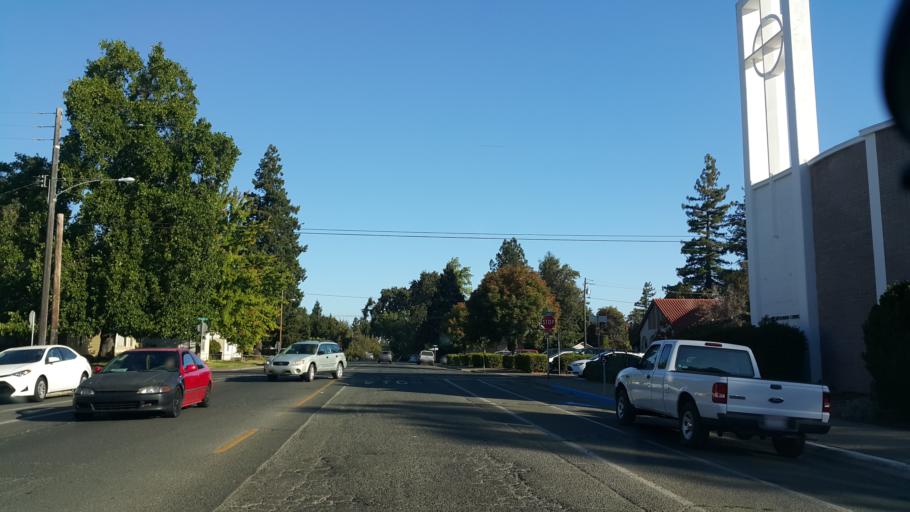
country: US
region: California
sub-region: Mendocino County
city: Ukiah
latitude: 39.1489
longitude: -123.2123
